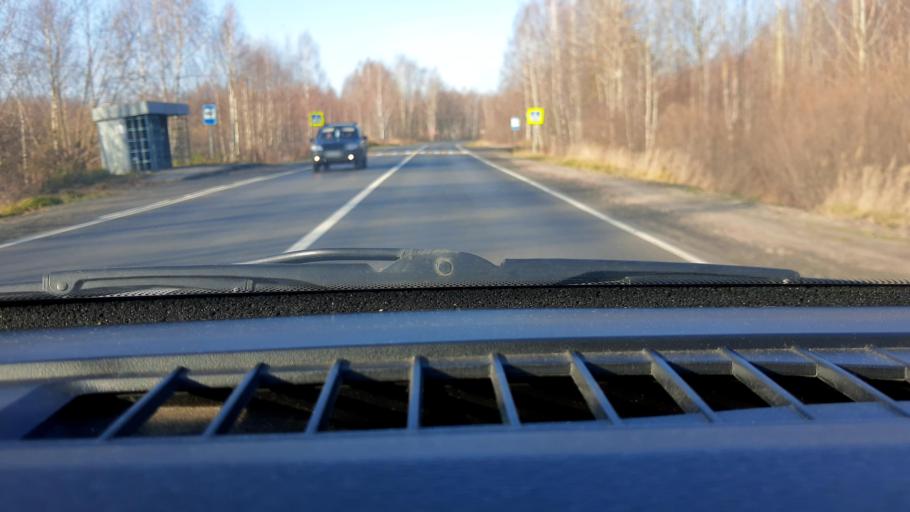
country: RU
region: Nizjnij Novgorod
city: Lukino
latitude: 56.5399
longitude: 43.7692
